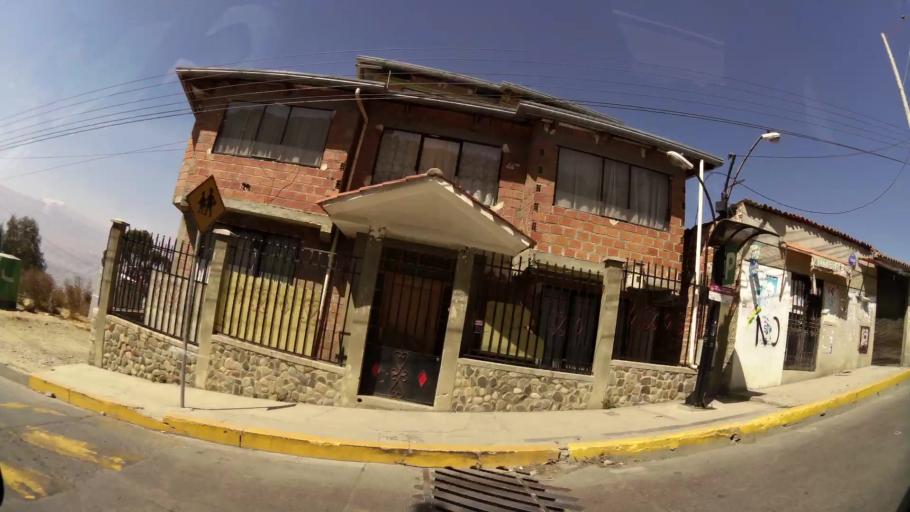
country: BO
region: La Paz
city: La Paz
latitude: -16.5325
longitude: -68.1424
